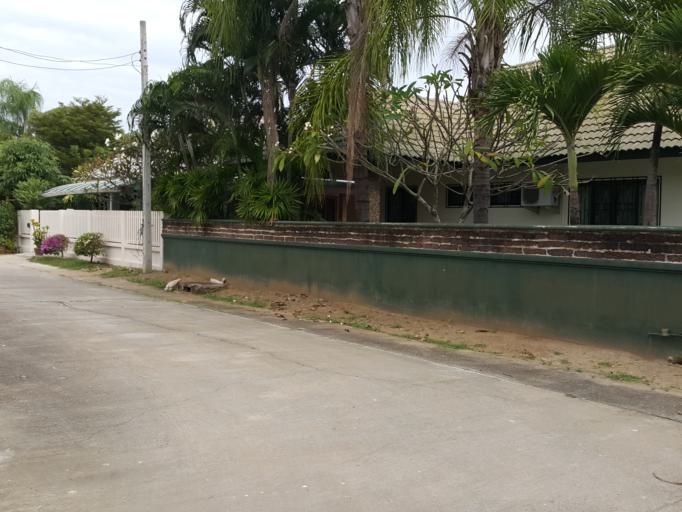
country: TH
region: Chiang Mai
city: San Kamphaeng
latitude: 18.7661
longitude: 99.1010
